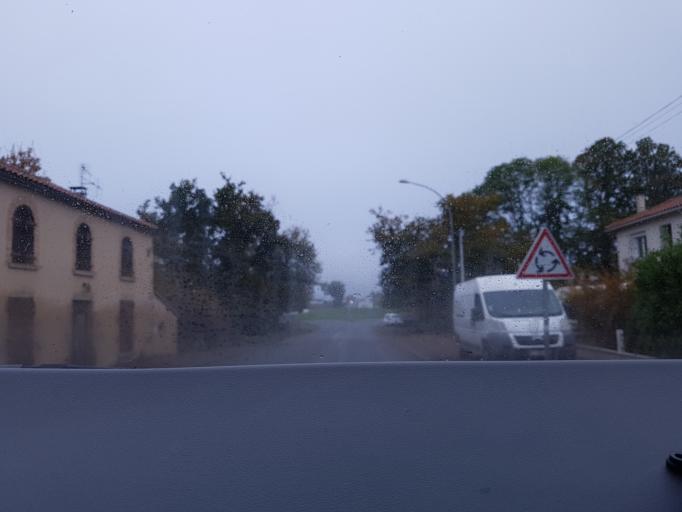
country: FR
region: Poitou-Charentes
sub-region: Departement des Deux-Sevres
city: Parthenay
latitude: 46.6635
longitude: -0.2504
